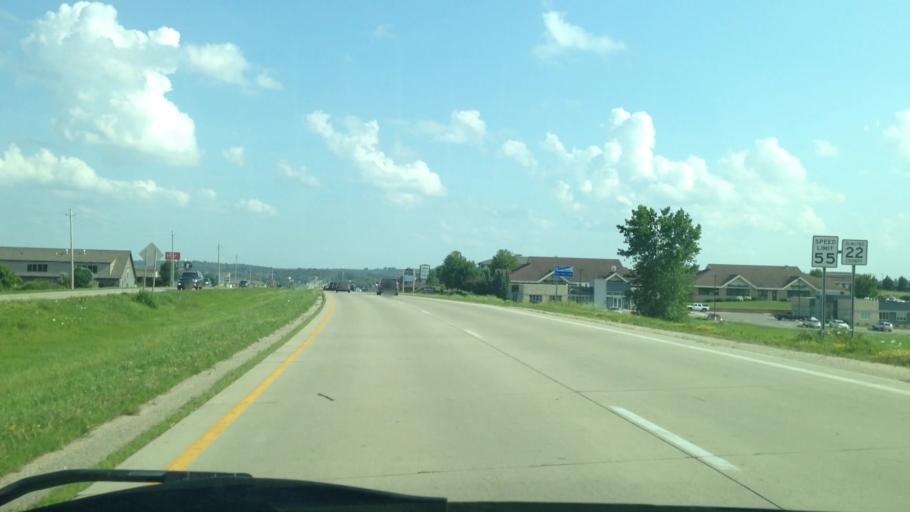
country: US
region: Minnesota
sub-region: Olmsted County
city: Rochester
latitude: 44.0558
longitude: -92.5238
